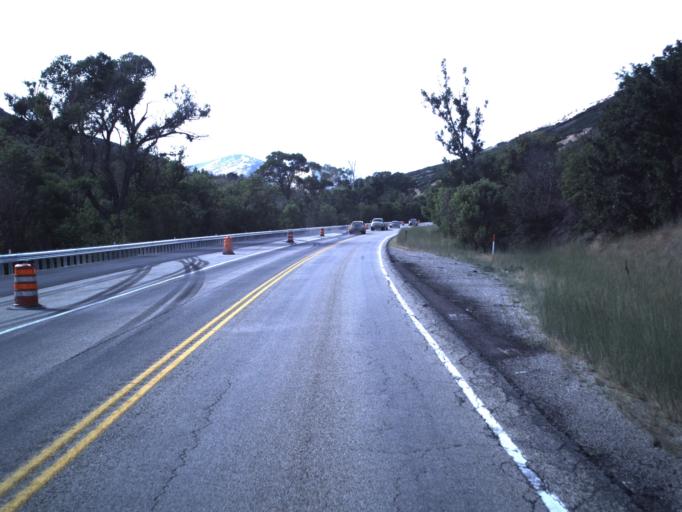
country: US
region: Utah
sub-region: Wasatch County
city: Heber
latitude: 40.4154
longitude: -111.3313
